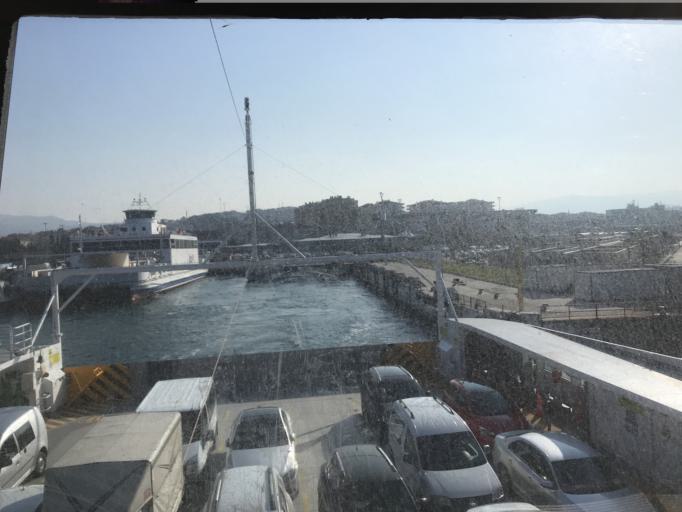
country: TR
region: Yalova
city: Yalova
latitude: 40.6618
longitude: 29.2793
